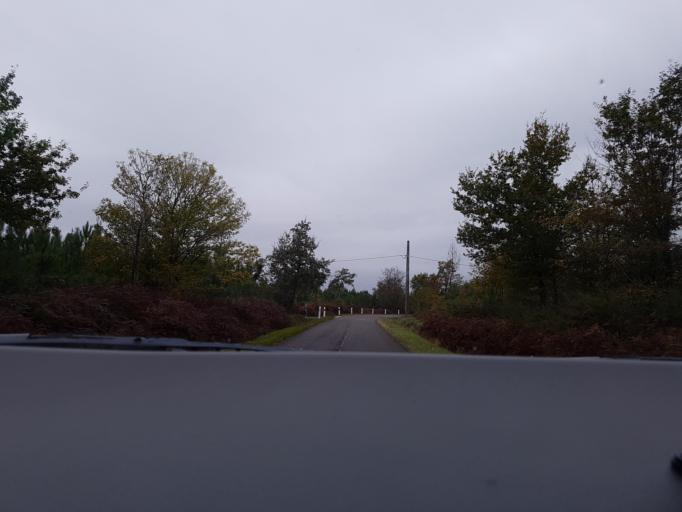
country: FR
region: Aquitaine
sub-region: Departement des Landes
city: Roquefort
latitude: 44.0849
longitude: -0.3890
